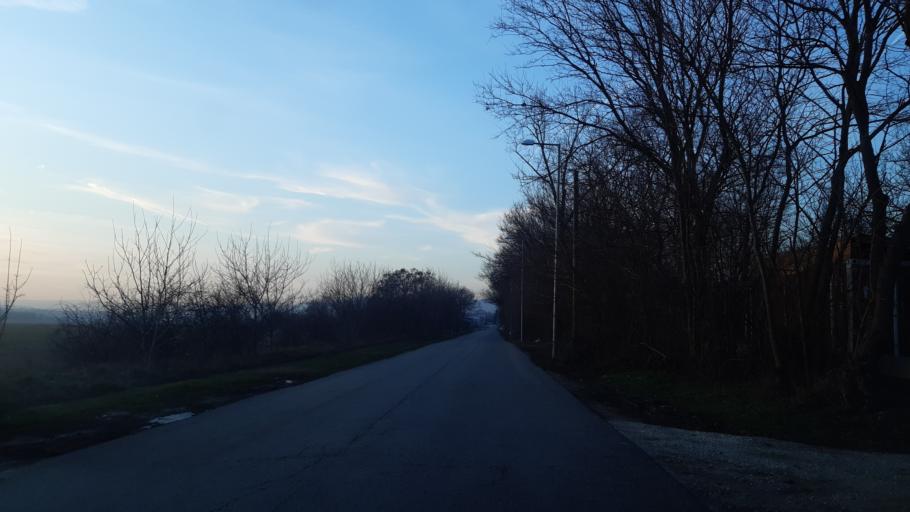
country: HU
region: Pest
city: Budaors
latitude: 47.4531
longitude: 18.9893
